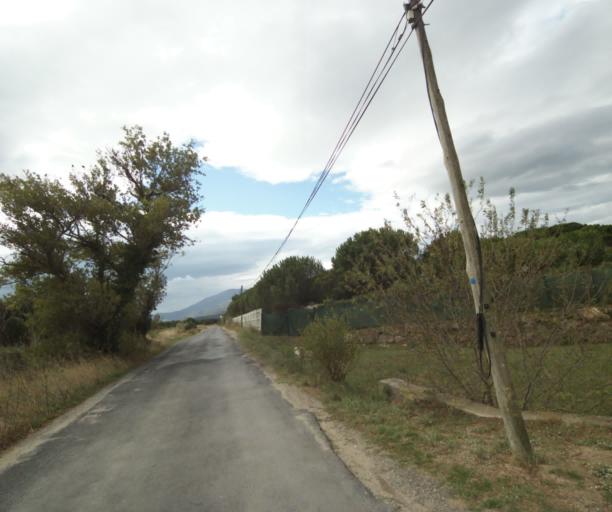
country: FR
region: Languedoc-Roussillon
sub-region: Departement des Pyrenees-Orientales
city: Argelers
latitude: 42.5740
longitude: 3.0411
